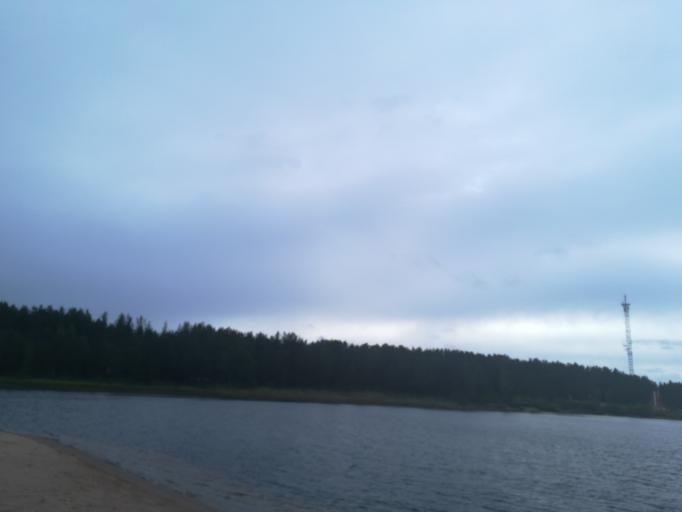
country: RU
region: Leningrad
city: Priozersk
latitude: 61.0443
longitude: 30.1833
